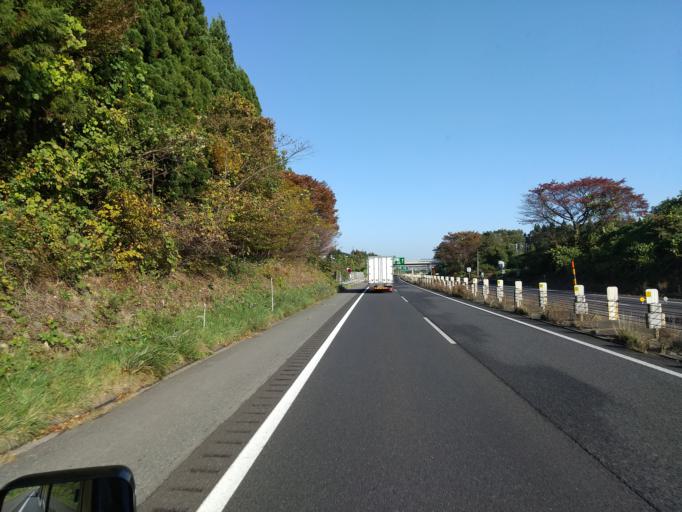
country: JP
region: Iwate
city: Kitakami
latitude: 39.2624
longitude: 141.0746
